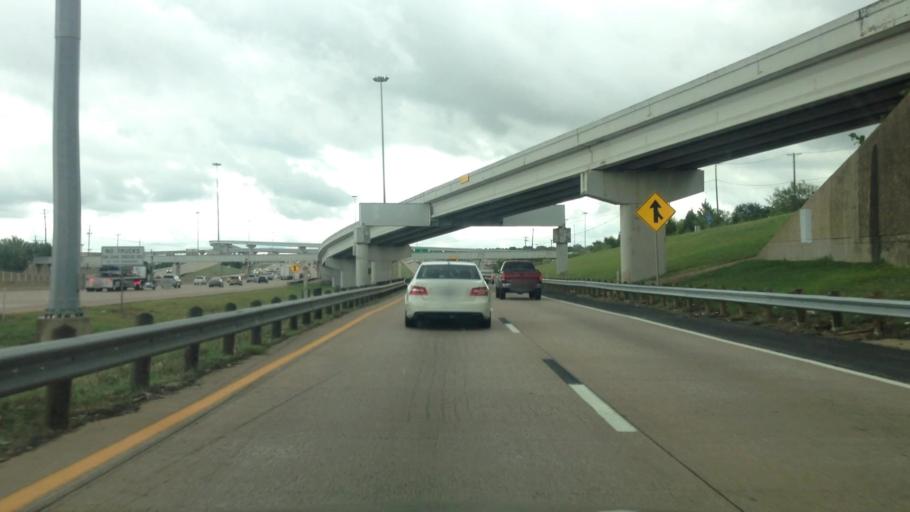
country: US
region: Texas
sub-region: Tarrant County
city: Edgecliff Village
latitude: 32.6646
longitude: -97.3300
